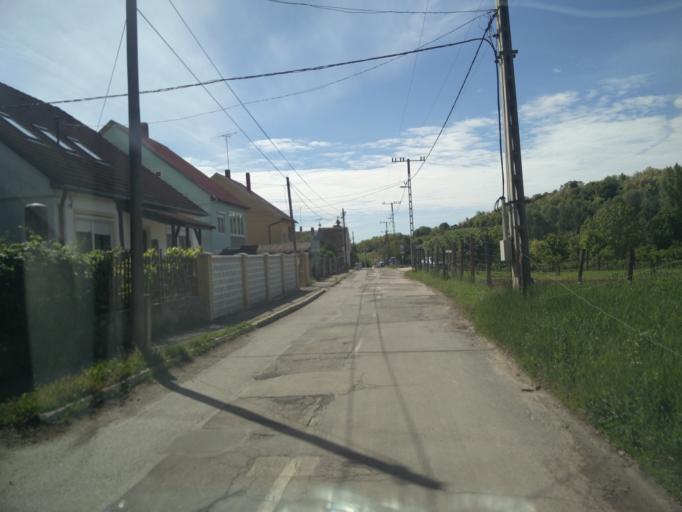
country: HU
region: Tolna
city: Szekszard
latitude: 46.3120
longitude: 18.6836
